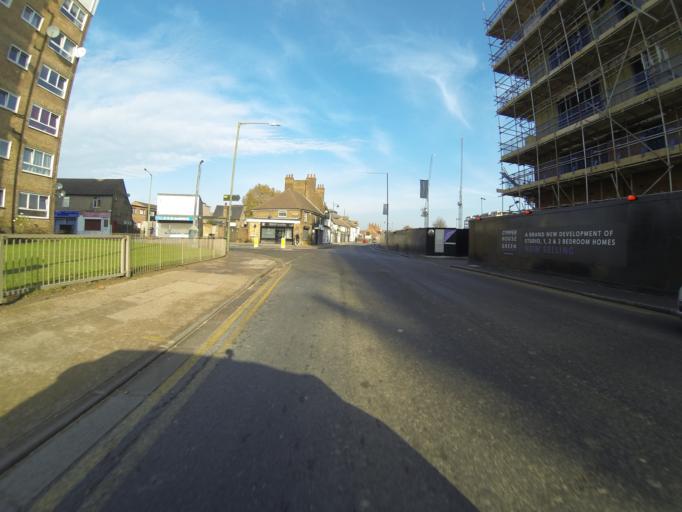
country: GB
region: England
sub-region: Kent
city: Dartford
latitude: 51.4409
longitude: 0.2154
